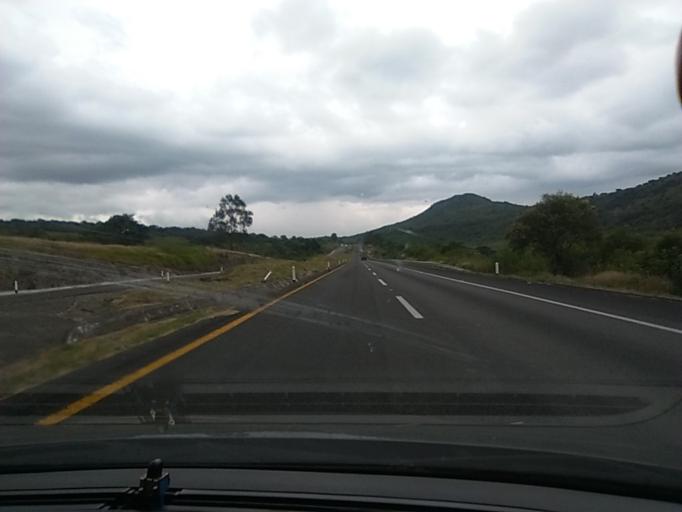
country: MX
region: Jalisco
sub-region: Zapotlan del Rey
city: Zapotlan del Rey
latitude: 20.5244
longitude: -102.9982
